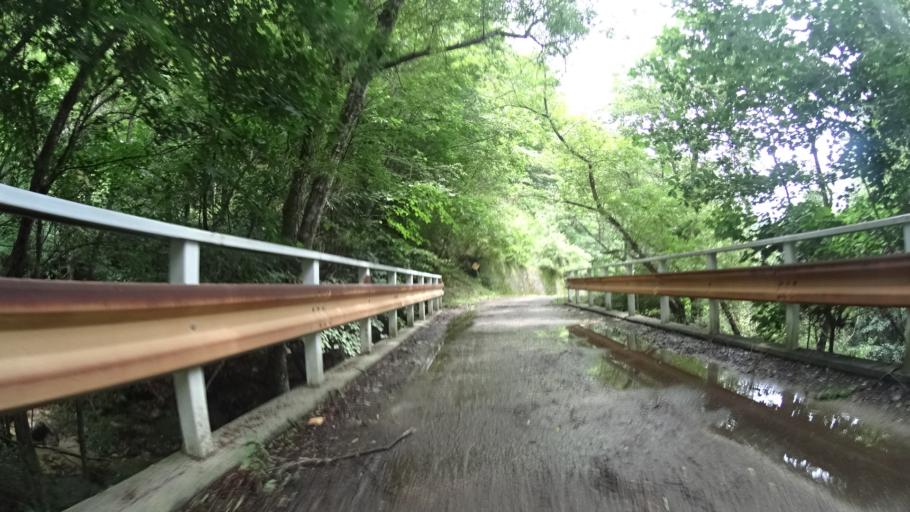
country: JP
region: Yamanashi
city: Kofu-shi
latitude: 35.8266
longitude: 138.5954
